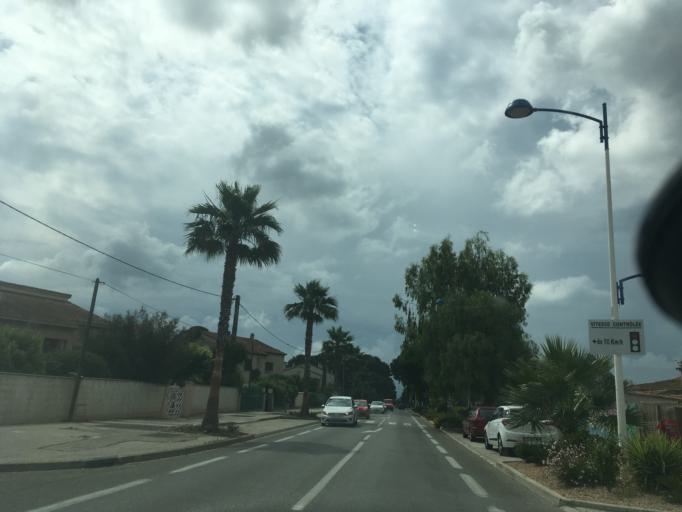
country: FR
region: Provence-Alpes-Cote d'Azur
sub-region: Departement du Var
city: La Londe-les-Maures
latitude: 43.1341
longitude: 6.2375
